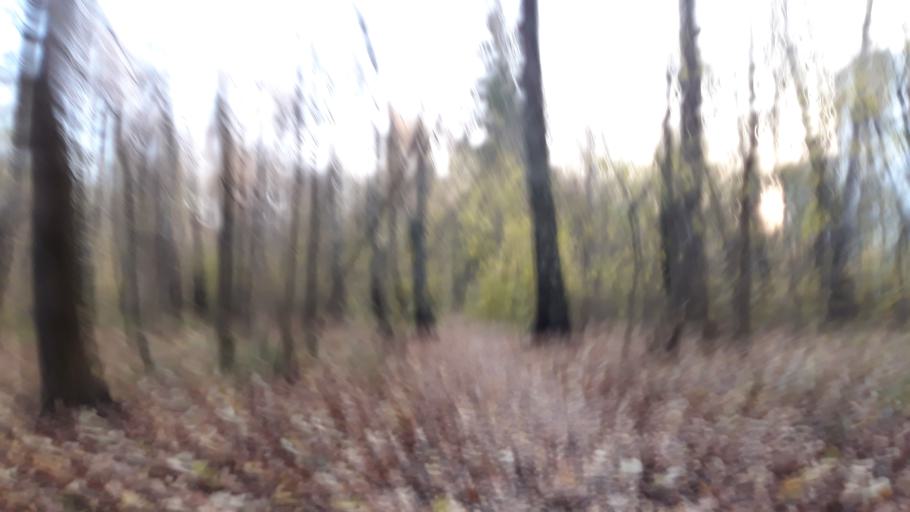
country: RU
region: Moscow
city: Zelenograd
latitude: 55.9959
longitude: 37.1983
